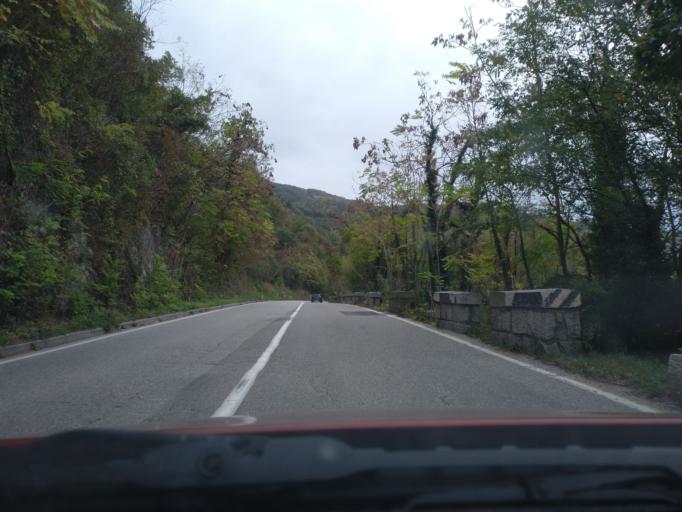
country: SI
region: Nova Gorica
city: Solkan
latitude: 45.9867
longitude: 13.6527
